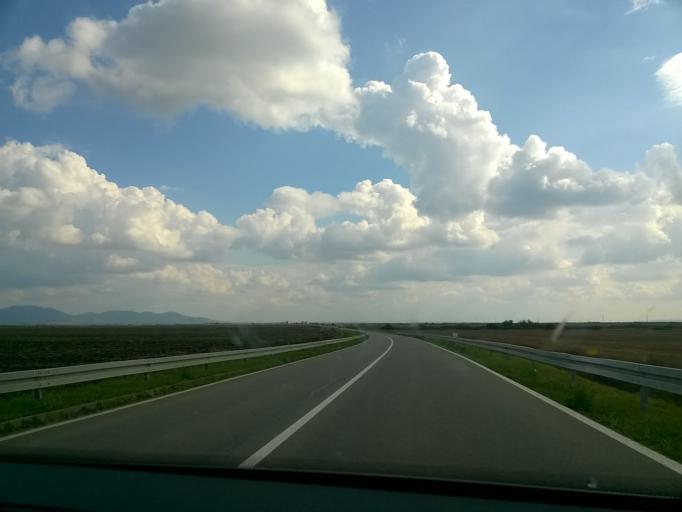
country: RS
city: Margita
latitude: 45.2050
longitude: 21.1827
